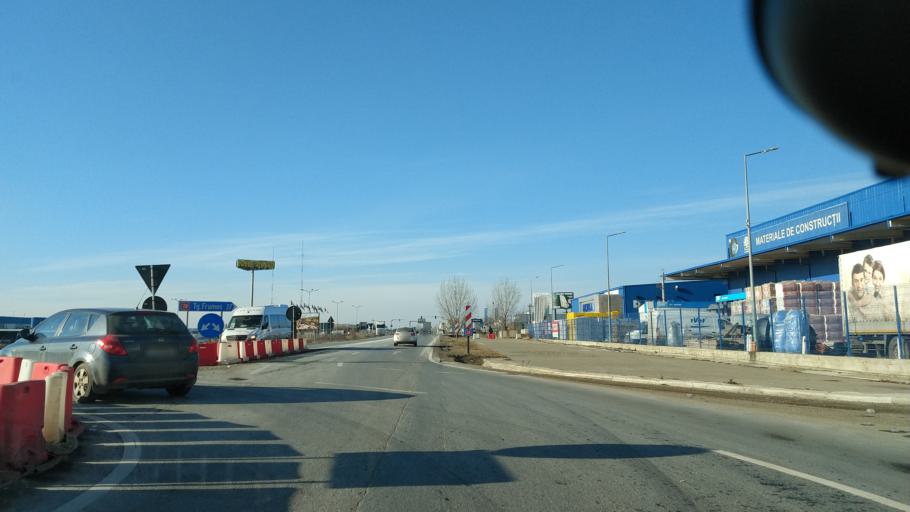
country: RO
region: Iasi
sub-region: Comuna Valea Lupului
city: Valea Lupului
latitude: 47.1811
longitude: 27.4725
